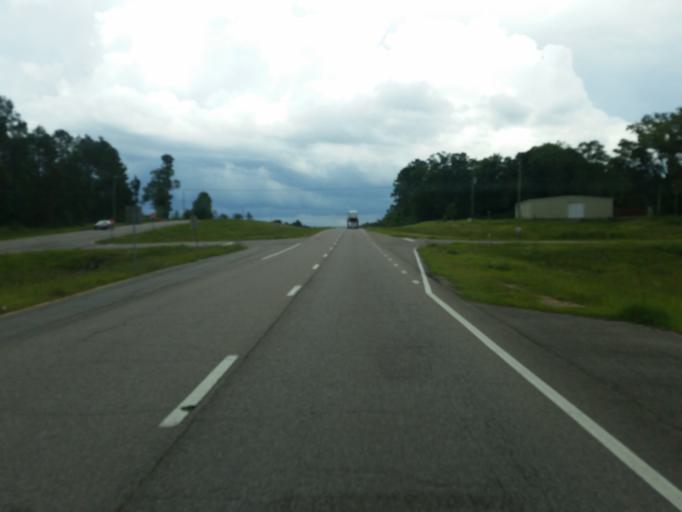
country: US
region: Mississippi
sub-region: George County
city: Lucedale
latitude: 30.8811
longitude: -88.4385
